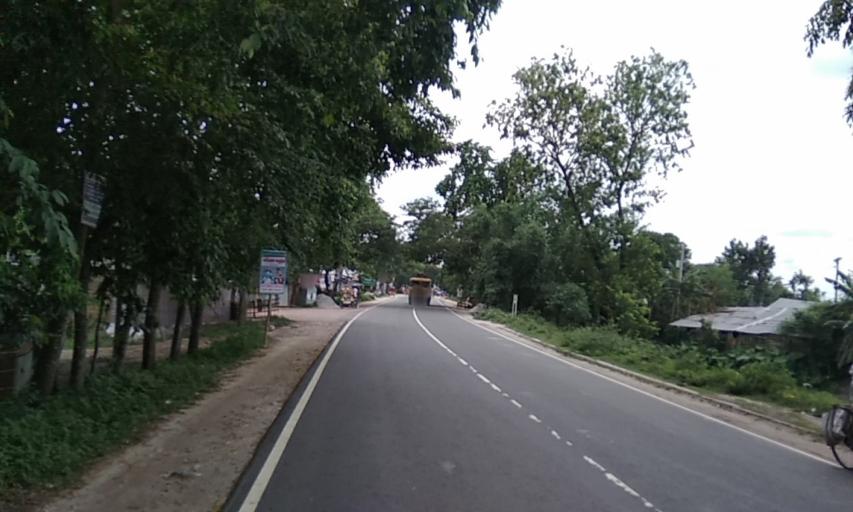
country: BD
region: Rangpur Division
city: Rangpur
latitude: 25.8009
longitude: 89.1891
